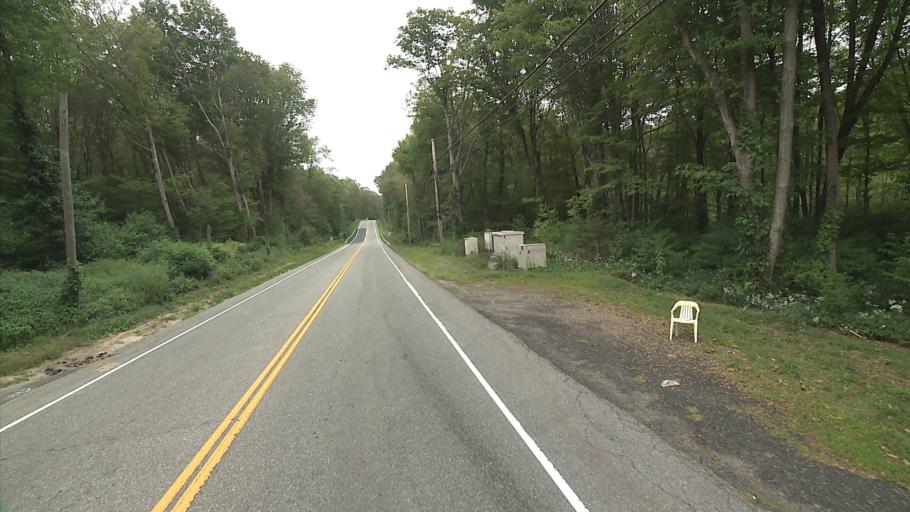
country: US
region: Connecticut
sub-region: Hartford County
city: Terramuggus
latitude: 41.7267
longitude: -72.4358
